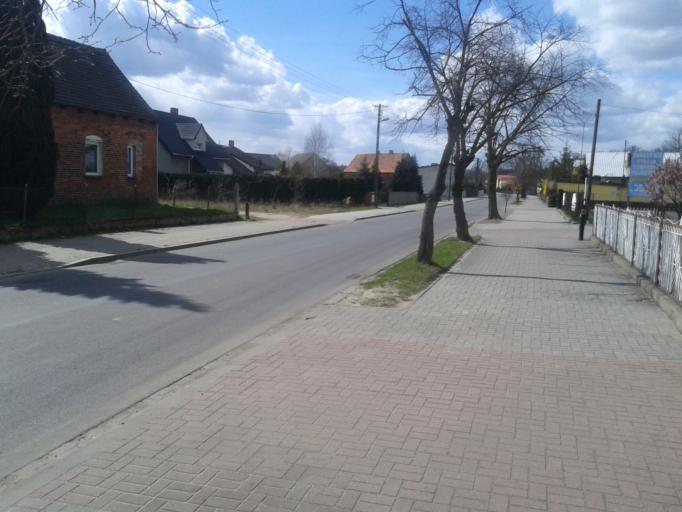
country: PL
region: Lower Silesian Voivodeship
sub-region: Powiat olesnicki
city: Miedzyborz
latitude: 51.3989
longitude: 17.6585
